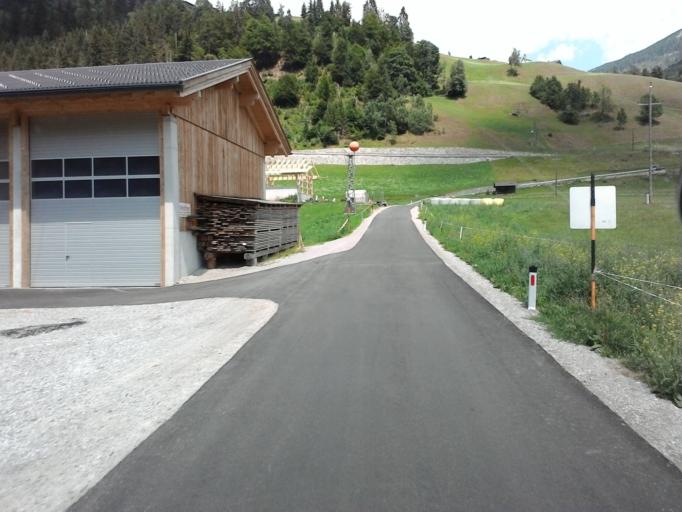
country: AT
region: Tyrol
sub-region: Politischer Bezirk Lienz
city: Untertilliach
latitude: 46.7010
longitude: 12.7713
